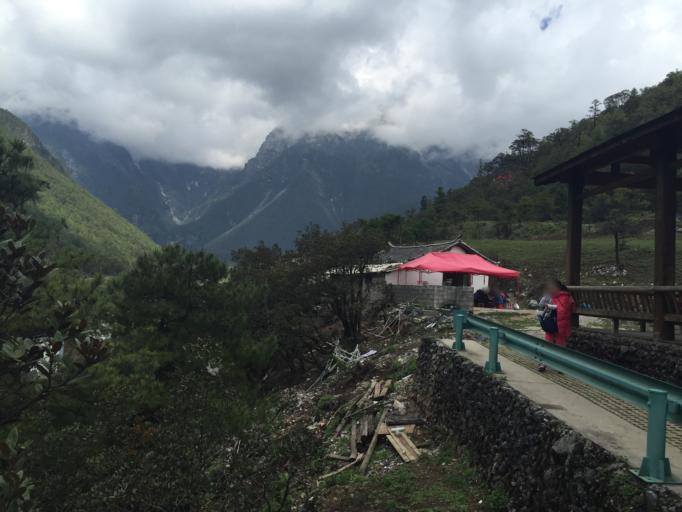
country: CN
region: Yunnan
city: Xiaqiaotou
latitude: 27.1297
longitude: 100.2465
